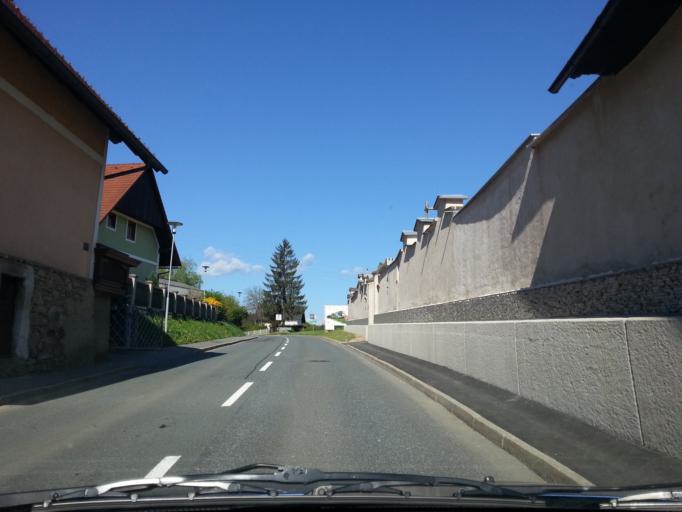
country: AT
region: Styria
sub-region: Politischer Bezirk Leibnitz
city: Arnfels
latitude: 46.6774
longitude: 15.3980
